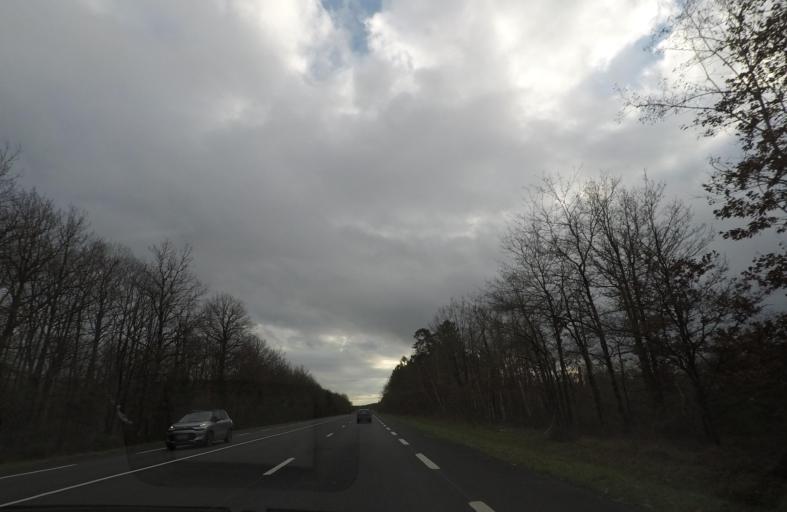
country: FR
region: Centre
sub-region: Departement du Loir-et-Cher
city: Soings-en-Sologne
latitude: 47.4529
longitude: 1.5315
